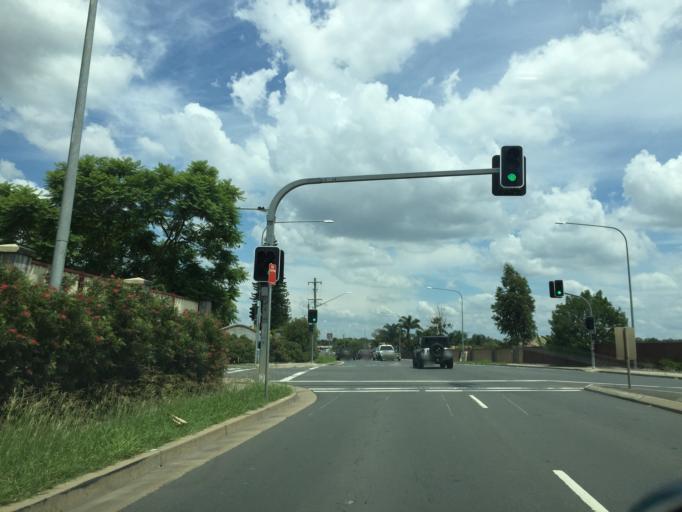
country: AU
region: New South Wales
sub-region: Blacktown
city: Hassall Grove
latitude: -33.7351
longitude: 150.8459
